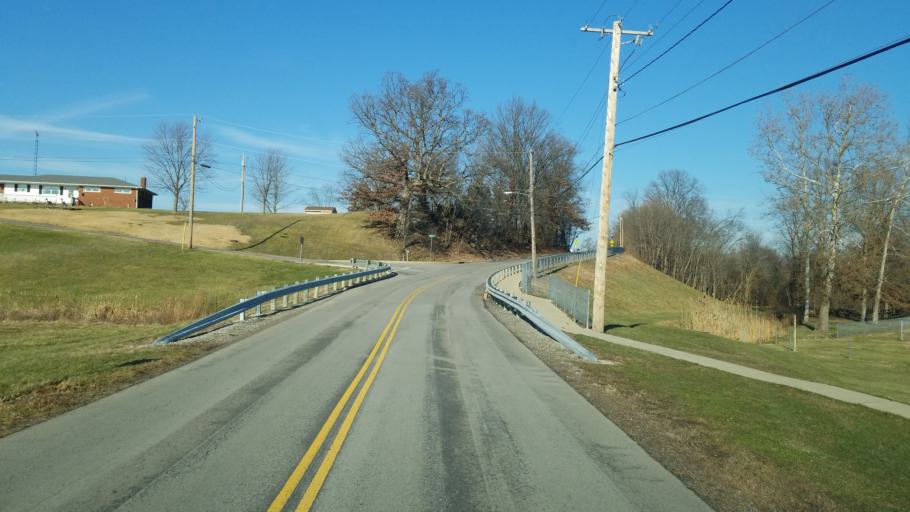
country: US
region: Ohio
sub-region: Huron County
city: Monroeville
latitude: 41.2497
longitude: -82.6956
